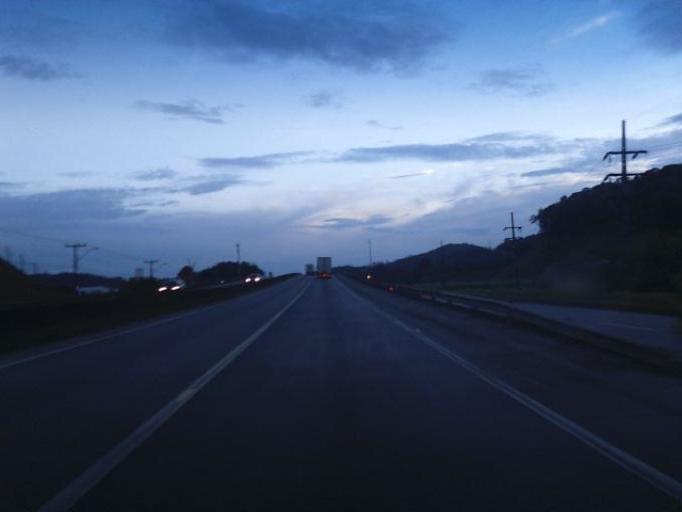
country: BR
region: Santa Catarina
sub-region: Joinville
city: Joinville
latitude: -26.2949
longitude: -48.8844
